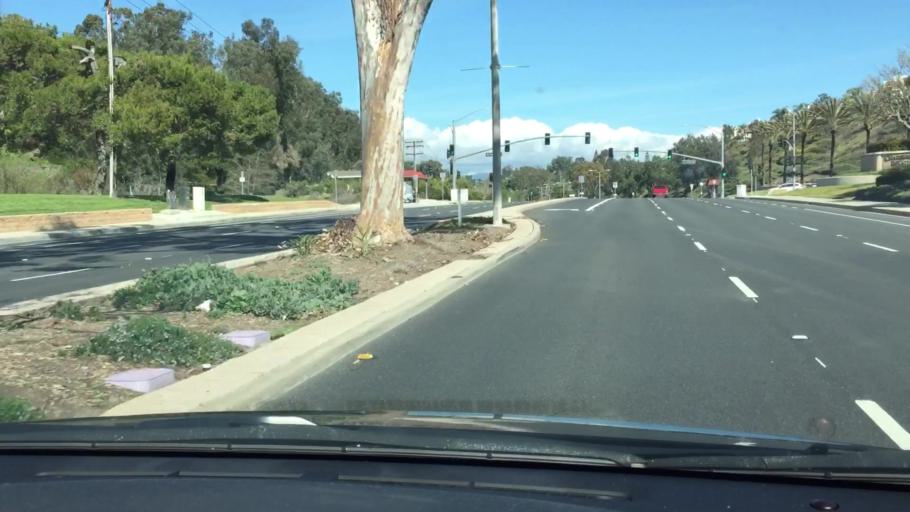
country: US
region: California
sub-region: Orange County
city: Laguna Niguel
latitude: 33.5303
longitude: -117.7066
